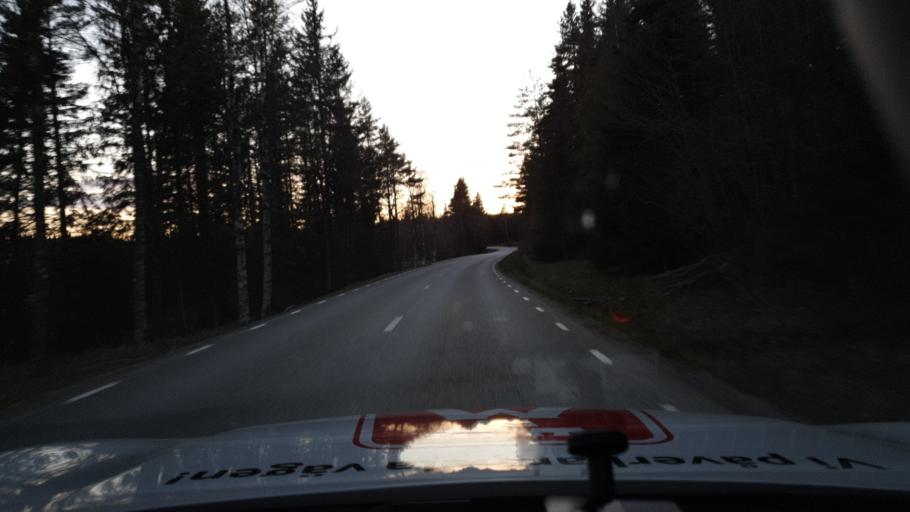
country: SE
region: OErebro
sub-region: Lindesbergs Kommun
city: Stora
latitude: 59.8996
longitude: 15.2169
